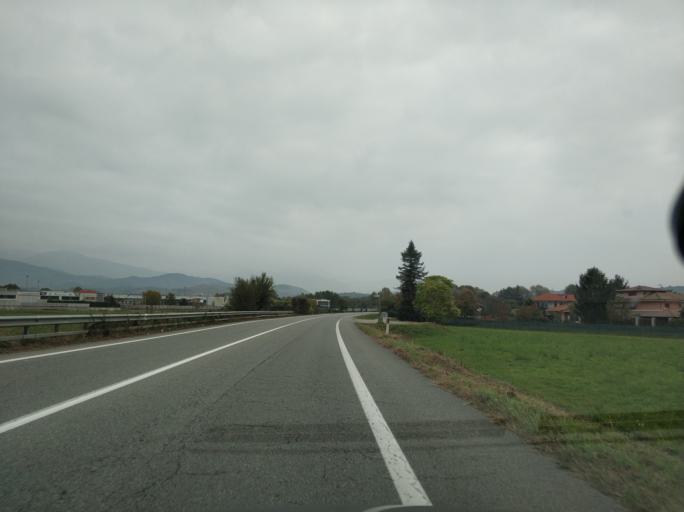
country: IT
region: Piedmont
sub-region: Provincia di Torino
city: Bairo
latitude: 45.3820
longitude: 7.7337
